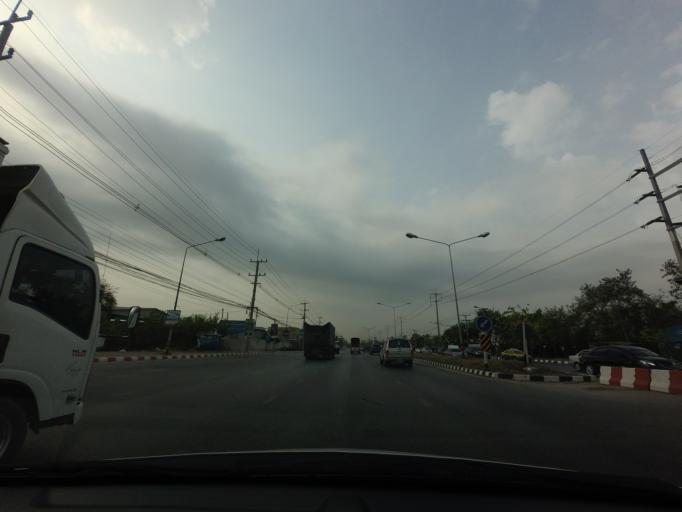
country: TH
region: Bangkok
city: Thawi Watthana
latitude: 13.7675
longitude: 100.3285
